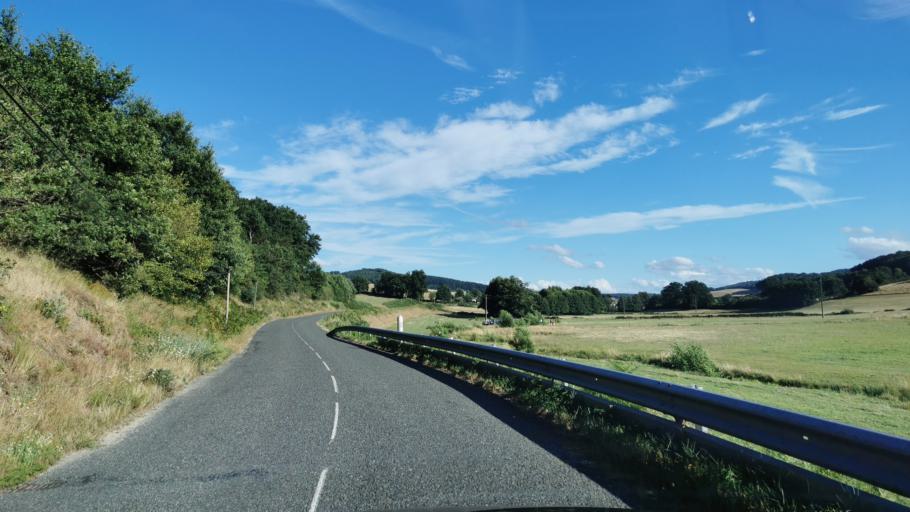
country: FR
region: Bourgogne
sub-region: Departement de Saone-et-Loire
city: Marmagne
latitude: 46.8283
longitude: 4.3187
